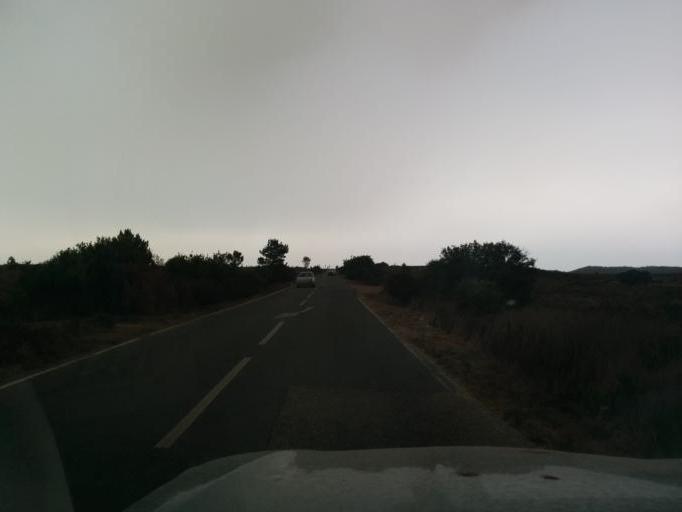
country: PT
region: Beja
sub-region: Odemira
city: Sao Teotonio
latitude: 37.5488
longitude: -8.7419
